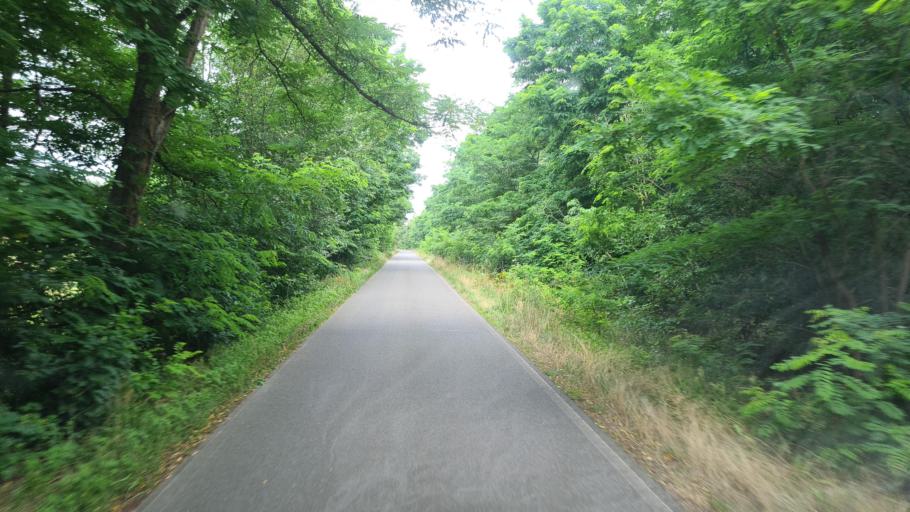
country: DE
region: Brandenburg
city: Neupetershain
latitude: 51.6752
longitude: 14.1163
